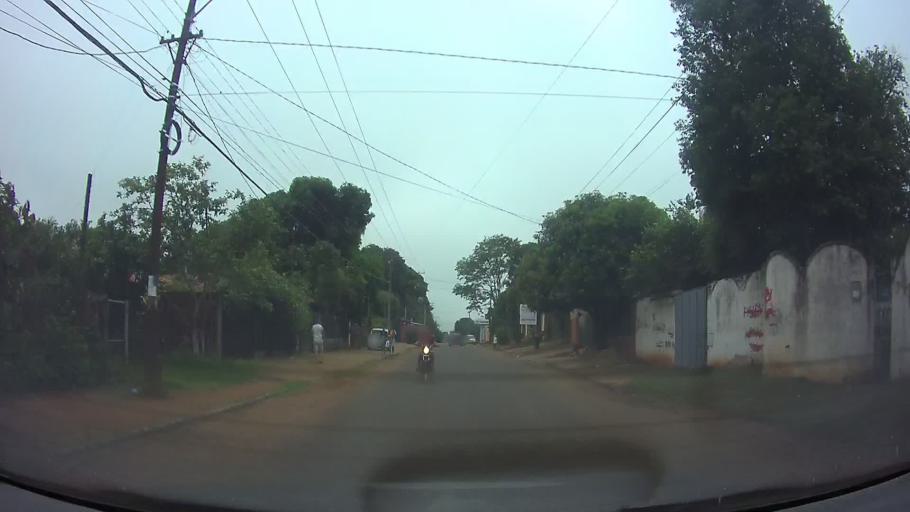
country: PY
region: Central
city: Itaugua
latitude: -25.3874
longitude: -57.3513
